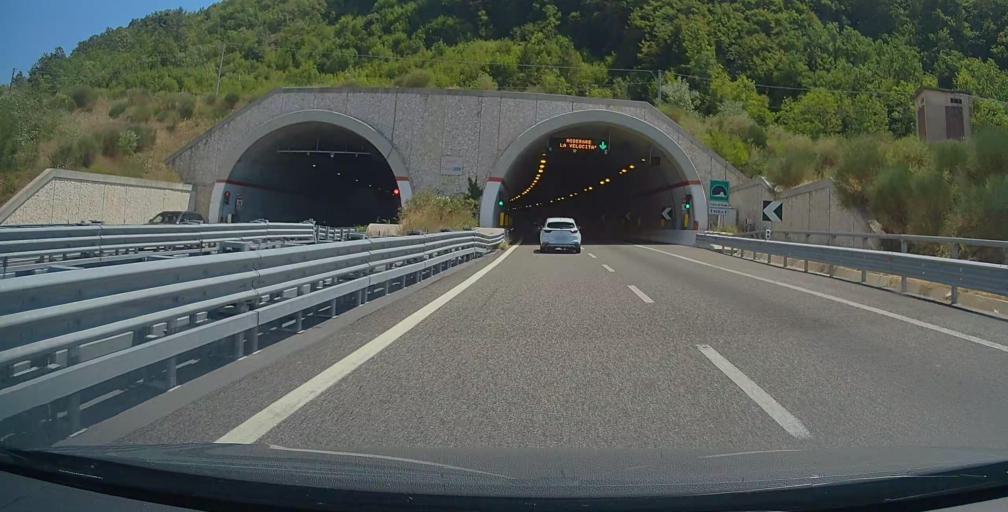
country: IT
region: Calabria
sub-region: Provincia di Cosenza
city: Mormanno
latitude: 39.9045
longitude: 15.9637
